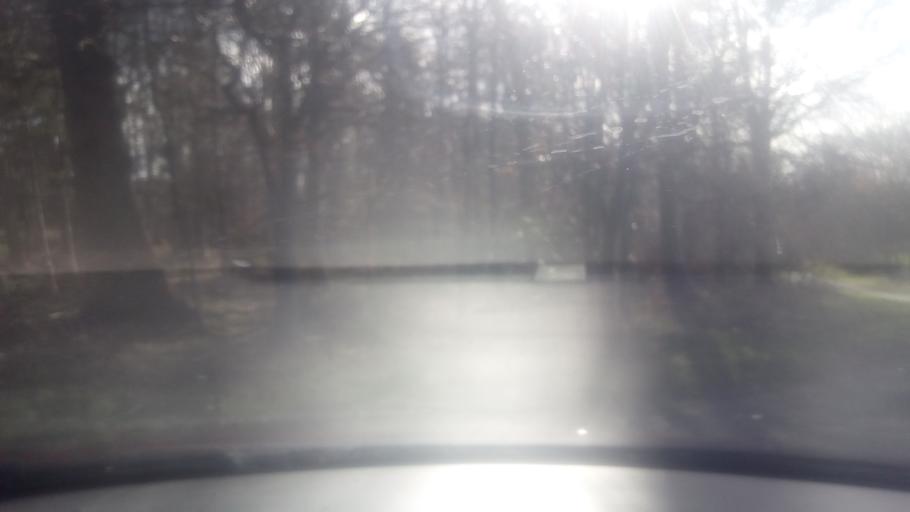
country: GB
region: Scotland
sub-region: The Scottish Borders
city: Jedburgh
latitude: 55.5171
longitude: -2.5696
